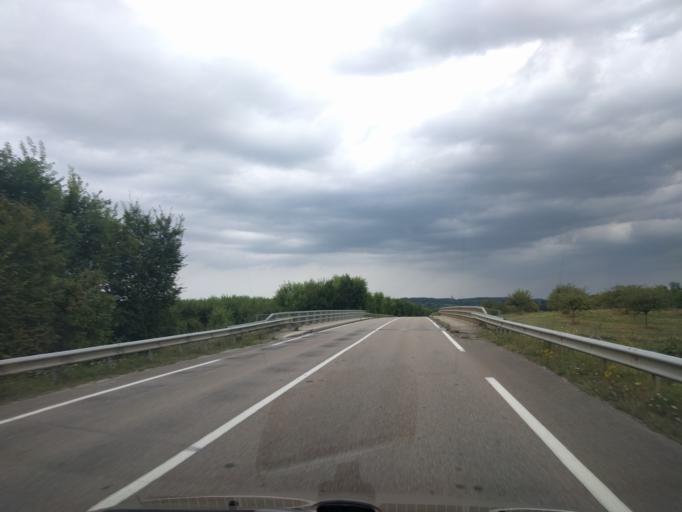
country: FR
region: Lower Normandy
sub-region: Departement de l'Orne
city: Gace
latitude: 48.7729
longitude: 0.3054
